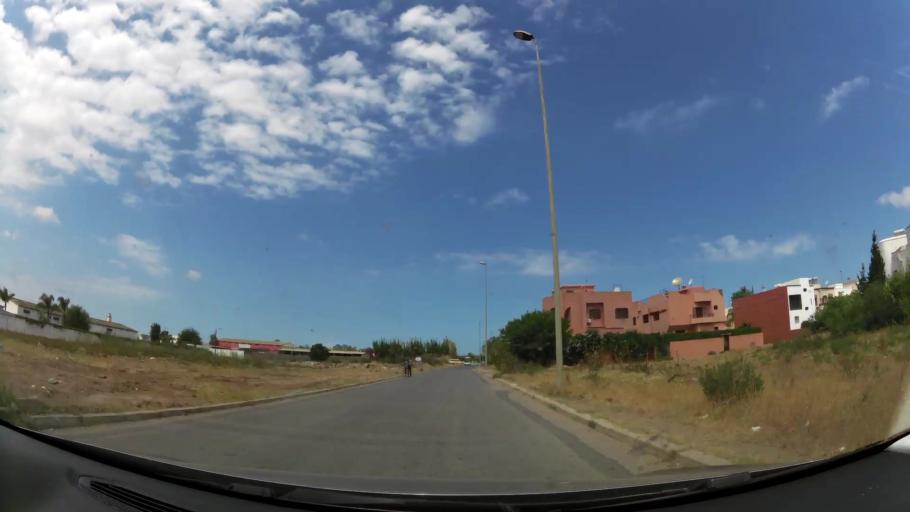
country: MA
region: Gharb-Chrarda-Beni Hssen
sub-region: Kenitra Province
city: Kenitra
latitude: 34.2414
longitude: -6.6063
